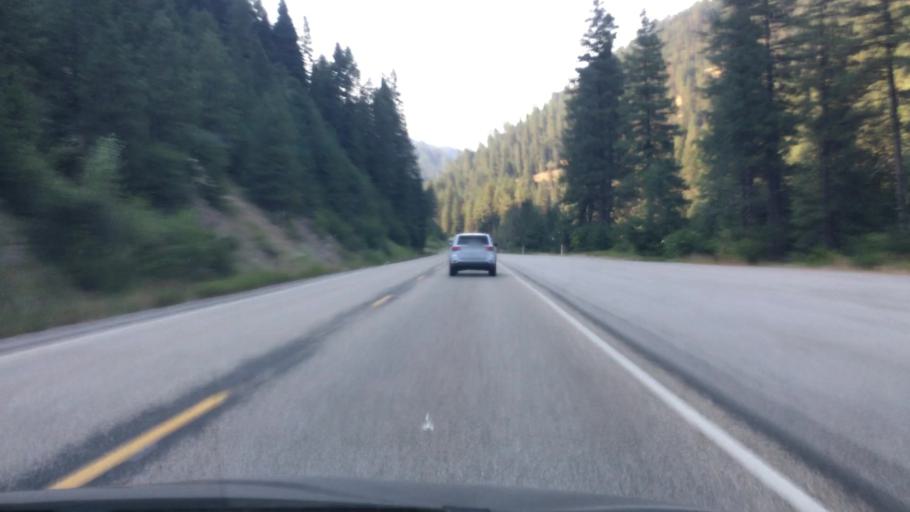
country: US
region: Idaho
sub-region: Valley County
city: Cascade
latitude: 44.1592
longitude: -116.1179
